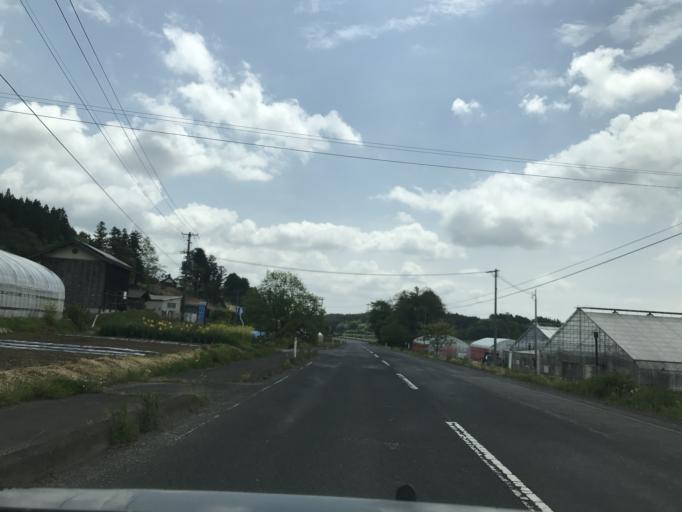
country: JP
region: Miyagi
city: Furukawa
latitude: 38.6851
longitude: 140.9549
